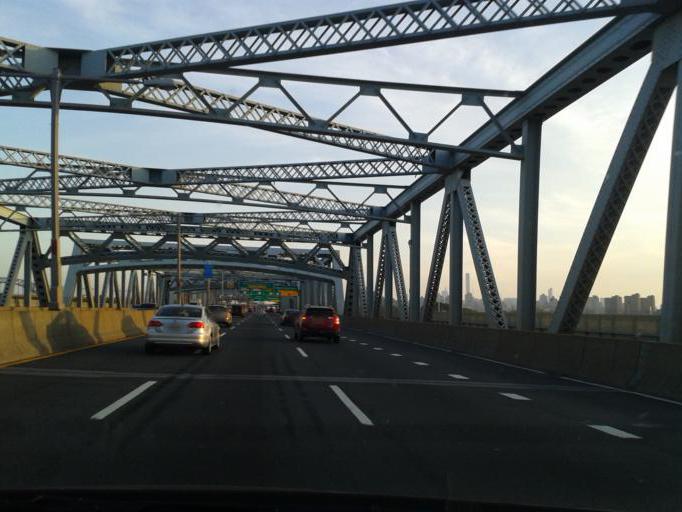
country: US
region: New York
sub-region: New York County
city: Manhattan
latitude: 40.8007
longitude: -73.9170
